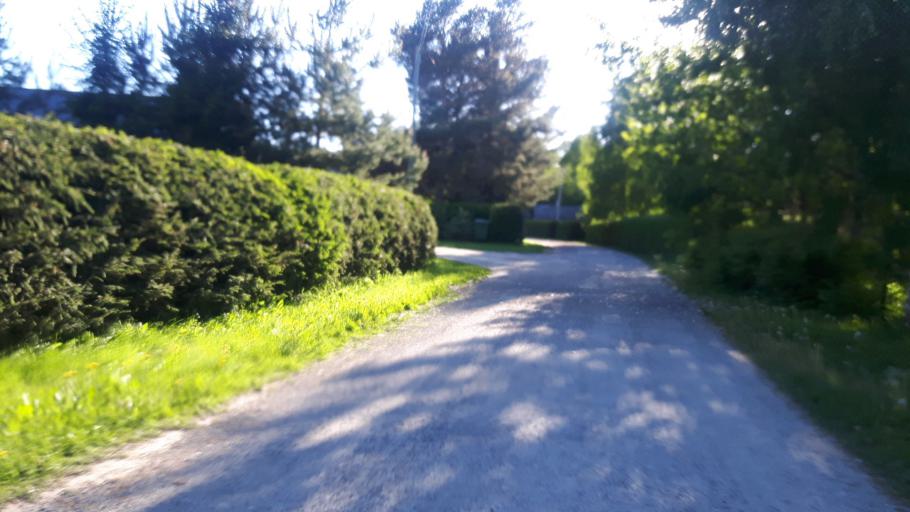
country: EE
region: Ida-Virumaa
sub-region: Kivioli linn
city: Kivioli
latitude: 59.4340
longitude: 26.9831
